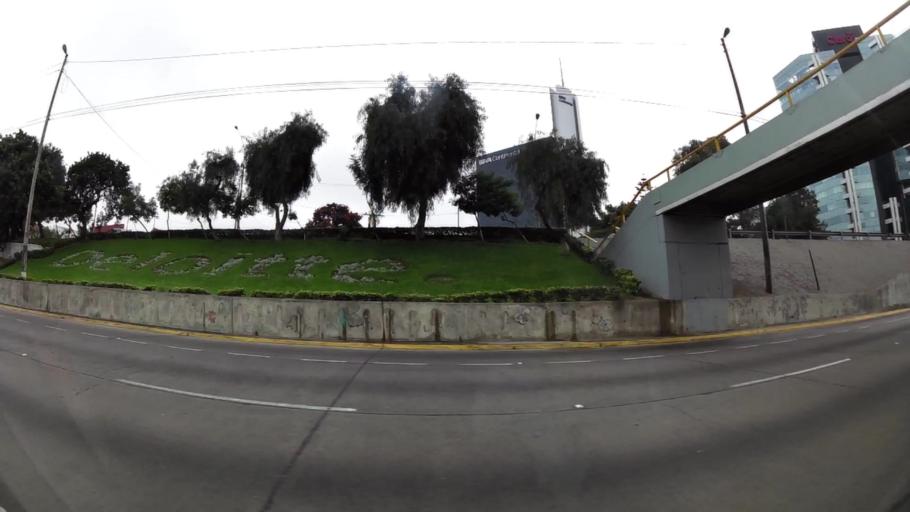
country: PE
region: Lima
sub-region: Lima
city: San Luis
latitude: -12.0922
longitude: -77.0229
